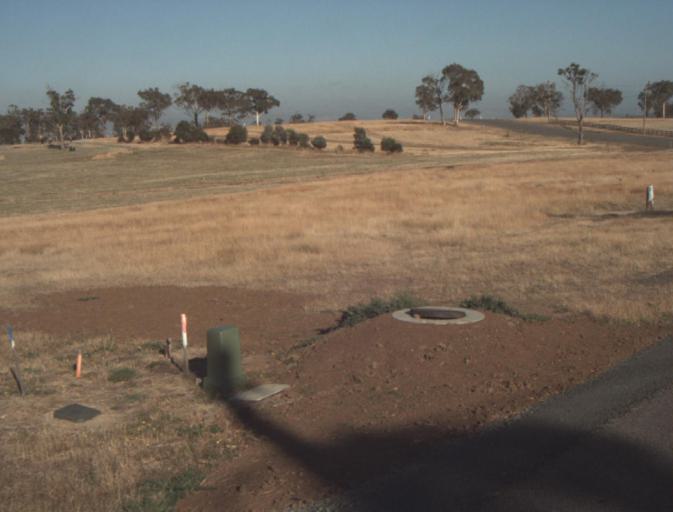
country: AU
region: Tasmania
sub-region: Launceston
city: Newstead
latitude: -41.4378
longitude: 147.2309
